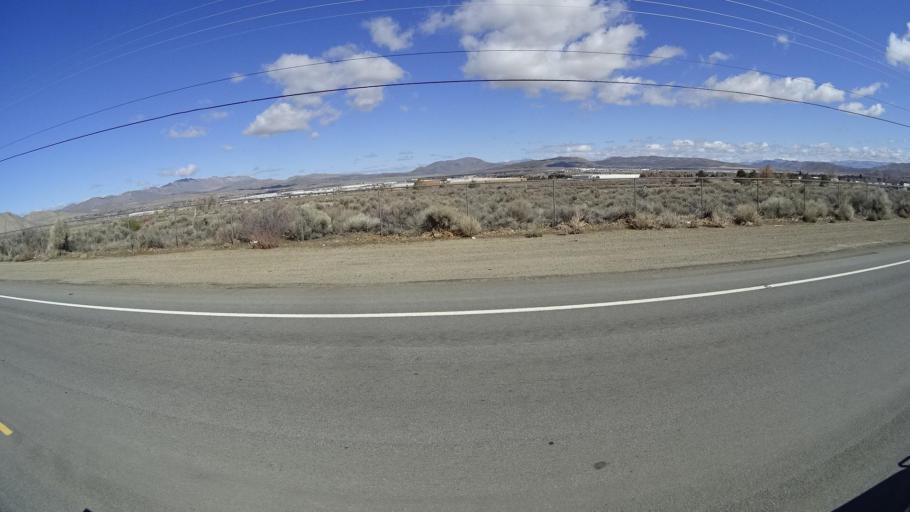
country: US
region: Nevada
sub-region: Washoe County
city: Lemmon Valley
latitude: 39.6251
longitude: -119.8888
